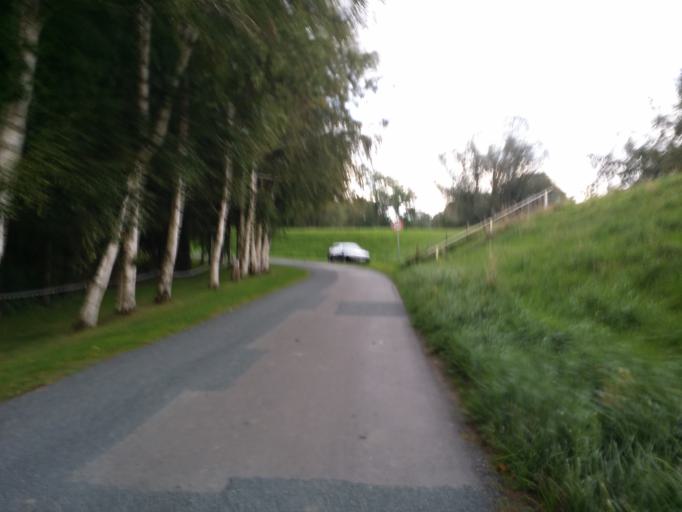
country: DE
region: Lower Saxony
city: Hemmoor
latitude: 53.7005
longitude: 9.1681
